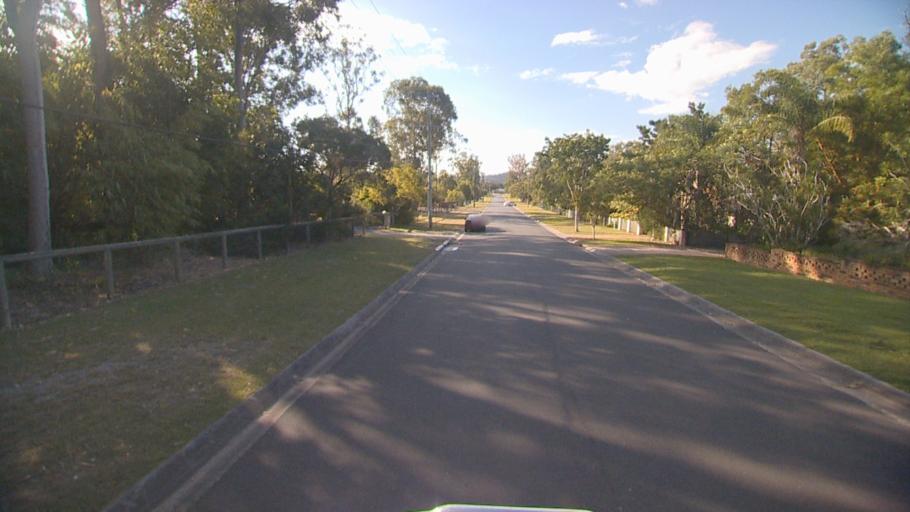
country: AU
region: Queensland
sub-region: Logan
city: Windaroo
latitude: -27.7575
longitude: 153.1916
